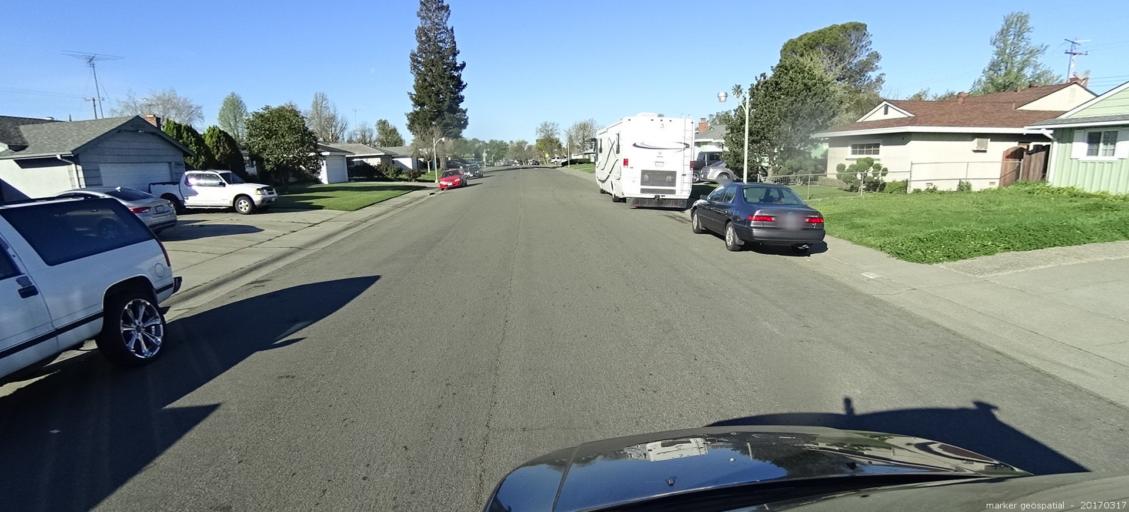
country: US
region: California
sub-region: Sacramento County
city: Parkway
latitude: 38.4933
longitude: -121.4942
